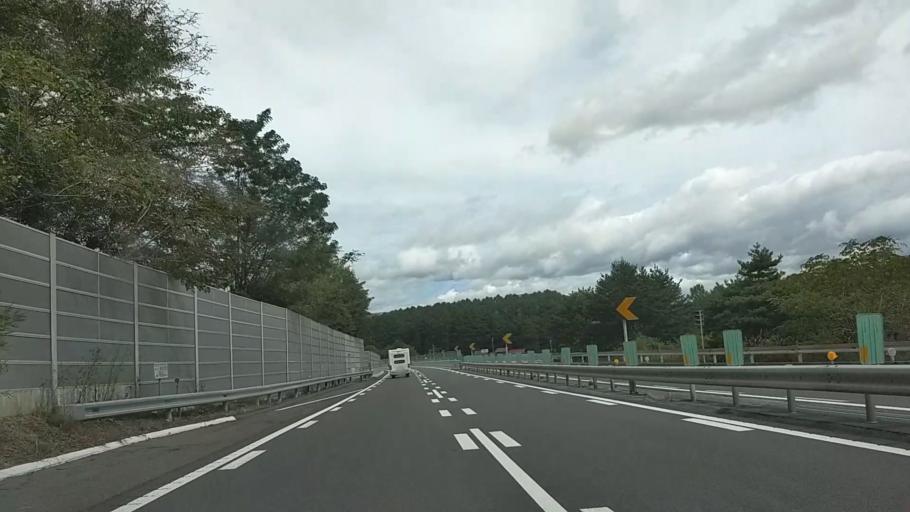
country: JP
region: Nagano
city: Chino
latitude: 35.9766
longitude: 138.1746
